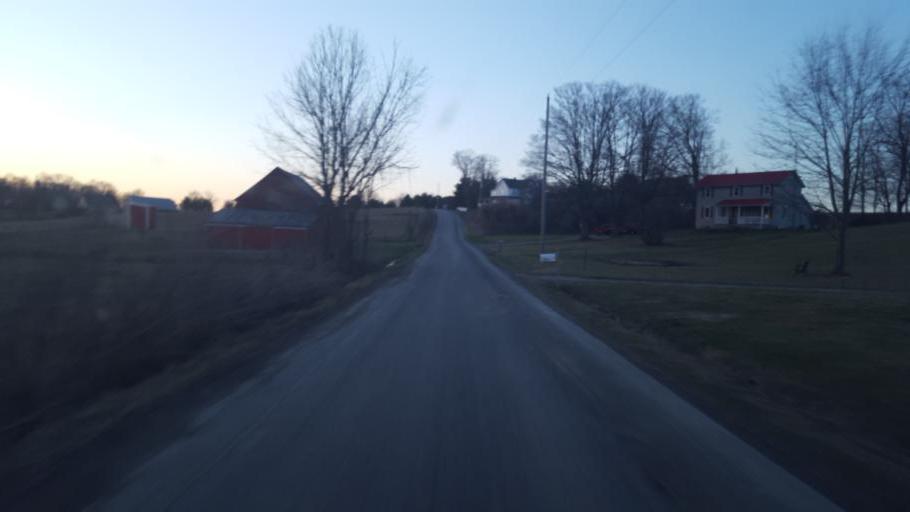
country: US
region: Ohio
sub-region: Knox County
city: Fredericktown
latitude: 40.5180
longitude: -82.6171
